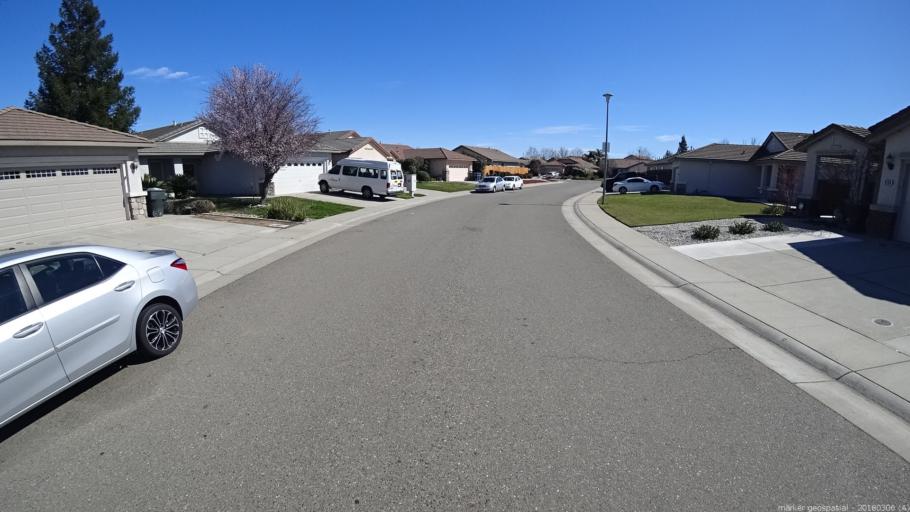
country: US
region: California
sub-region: Sacramento County
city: Vineyard
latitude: 38.4693
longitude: -121.3611
